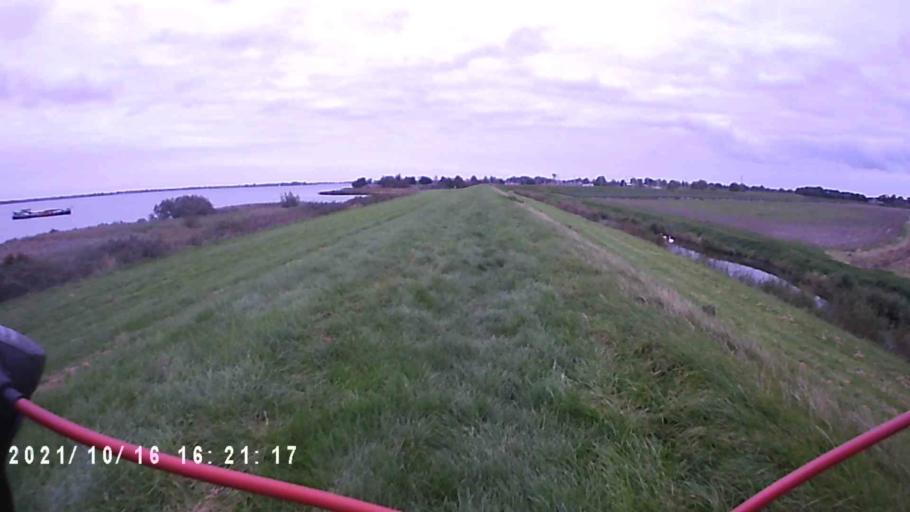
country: NL
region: Friesland
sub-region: Gemeente Dongeradeel
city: Anjum
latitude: 53.3882
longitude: 6.1555
